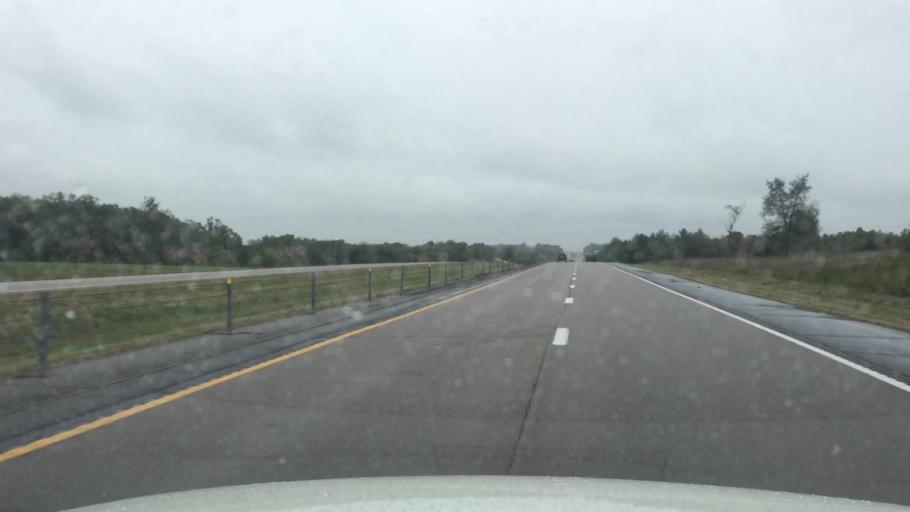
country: US
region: Missouri
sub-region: Boone County
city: Ashland
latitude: 38.7137
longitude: -92.2546
